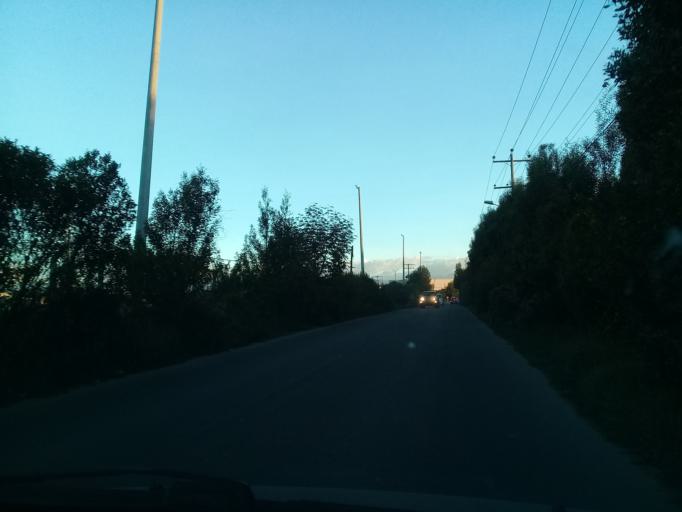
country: CO
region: Cundinamarca
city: Cota
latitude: 4.7653
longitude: -74.1544
